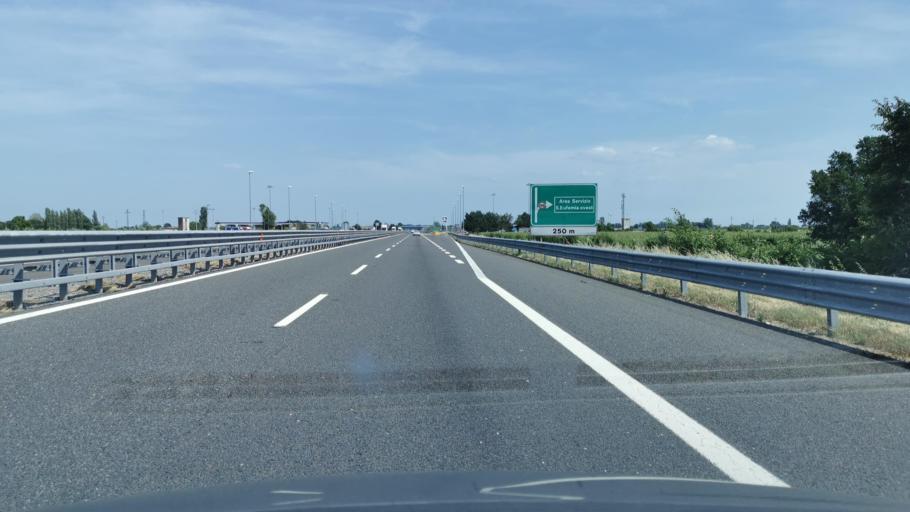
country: IT
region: Emilia-Romagna
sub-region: Provincia di Ravenna
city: Russi
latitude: 44.4035
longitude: 12.0398
